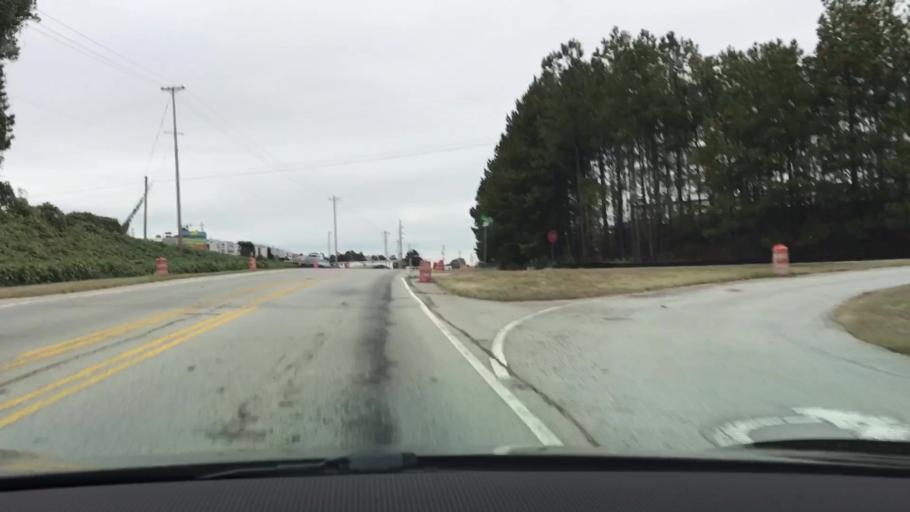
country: US
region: Georgia
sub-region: Gwinnett County
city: Buford
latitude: 34.1510
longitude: -83.9816
